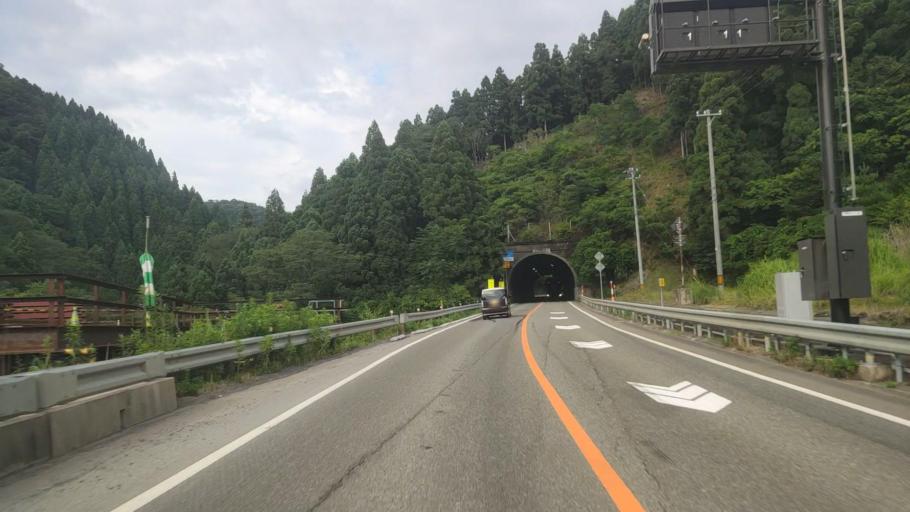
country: JP
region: Fukui
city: Takefu
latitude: 35.8238
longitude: 136.1046
